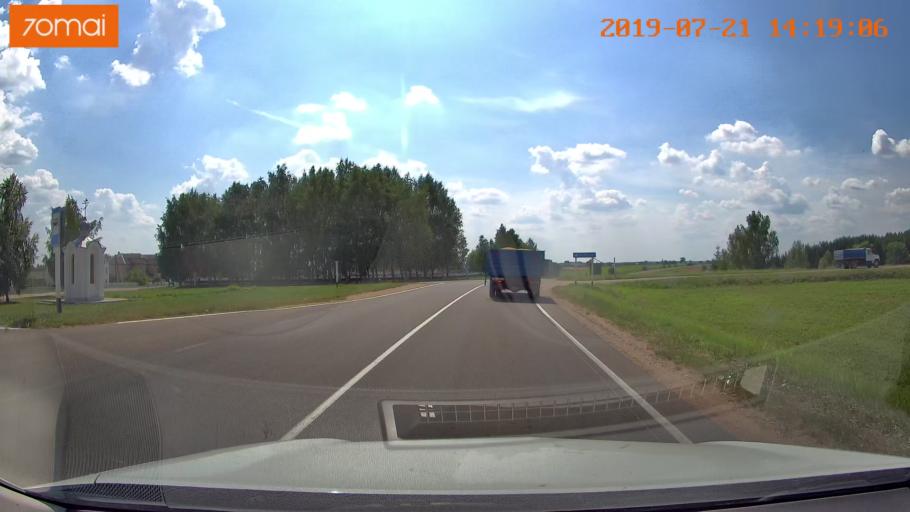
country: BY
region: Grodnenskaya
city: Karelichy
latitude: 53.5898
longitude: 26.1755
